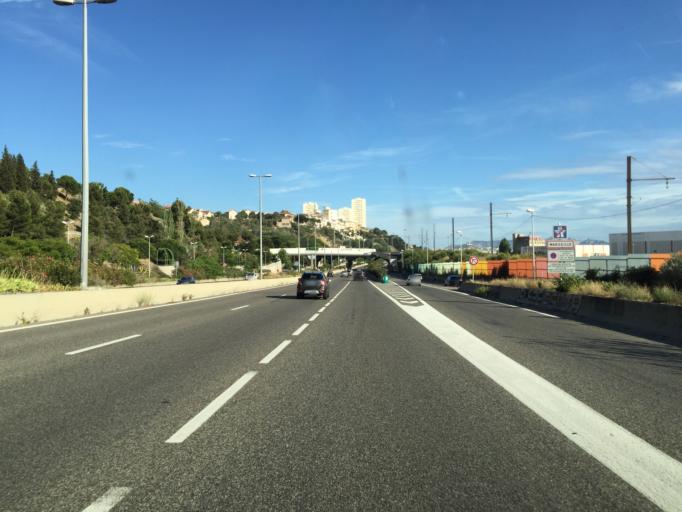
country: FR
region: Provence-Alpes-Cote d'Azur
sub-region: Departement des Bouches-du-Rhone
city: Marseille 16
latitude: 43.3458
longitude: 5.3456
